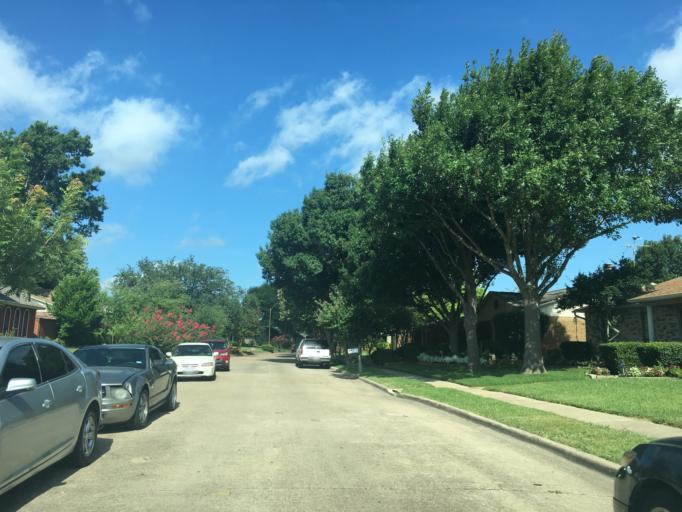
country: US
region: Texas
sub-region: Dallas County
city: Garland
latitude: 32.8507
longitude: -96.6619
